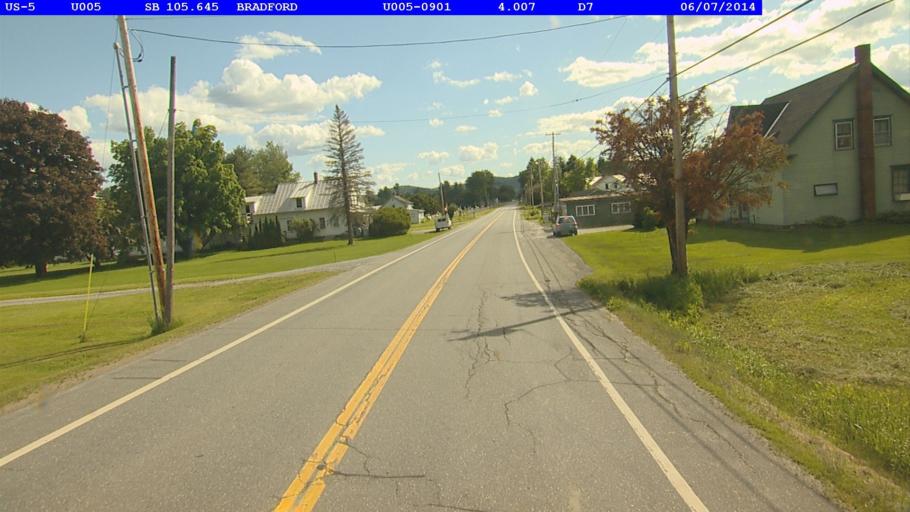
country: US
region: New Hampshire
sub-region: Grafton County
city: Haverhill
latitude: 44.0104
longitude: -72.1077
